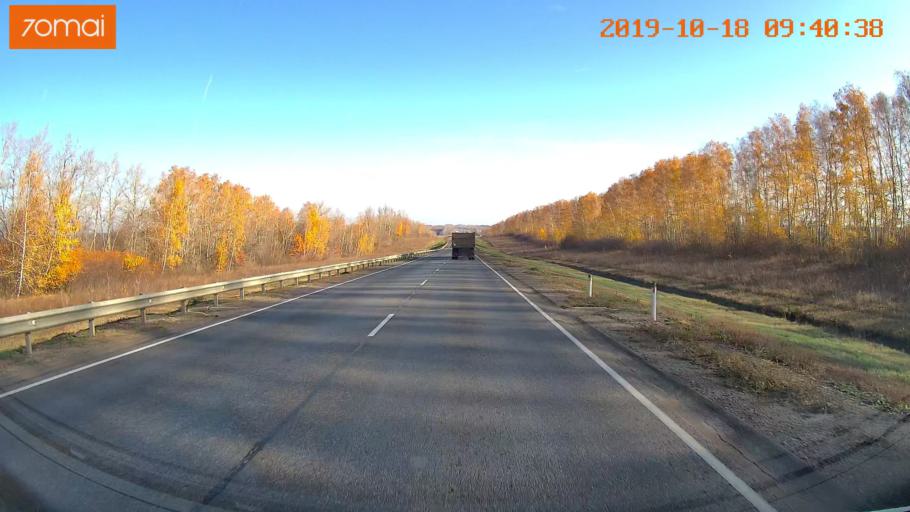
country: RU
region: Tula
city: Kazachka
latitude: 53.2662
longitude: 38.1509
